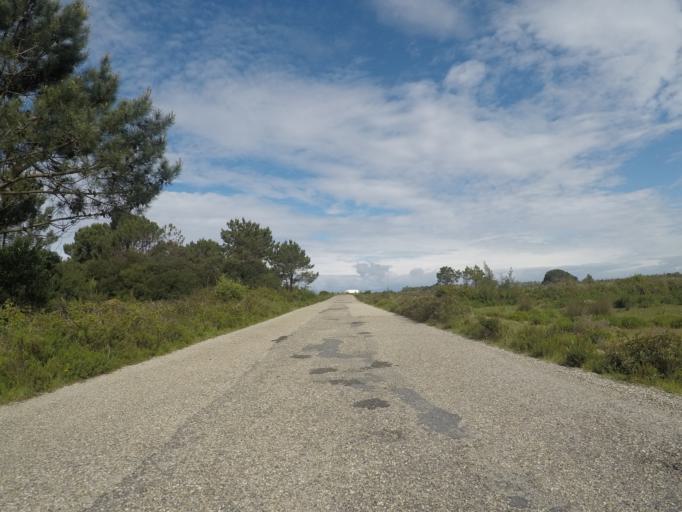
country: PT
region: Beja
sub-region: Odemira
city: Sao Teotonio
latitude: 37.4484
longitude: -8.7643
